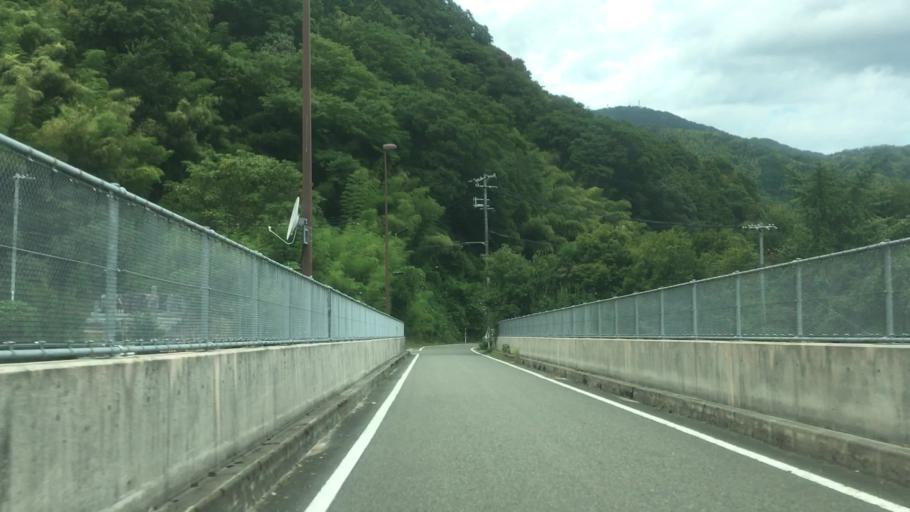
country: JP
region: Hyogo
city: Toyooka
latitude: 35.5867
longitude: 134.7989
